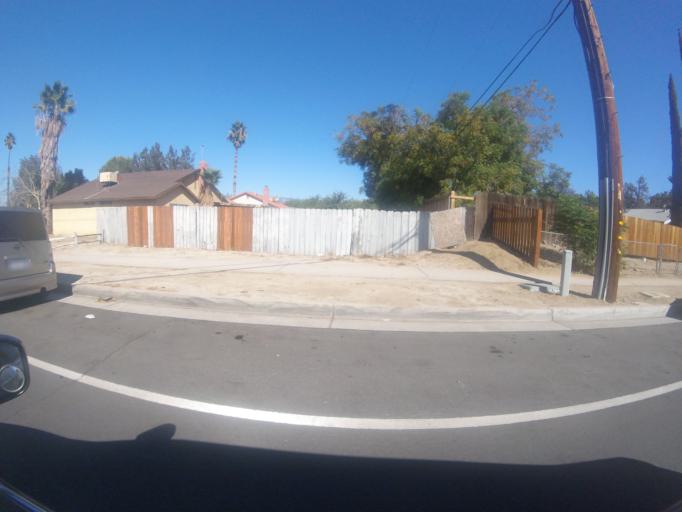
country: US
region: California
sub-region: San Bernardino County
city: Redlands
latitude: 34.0736
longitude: -117.1804
